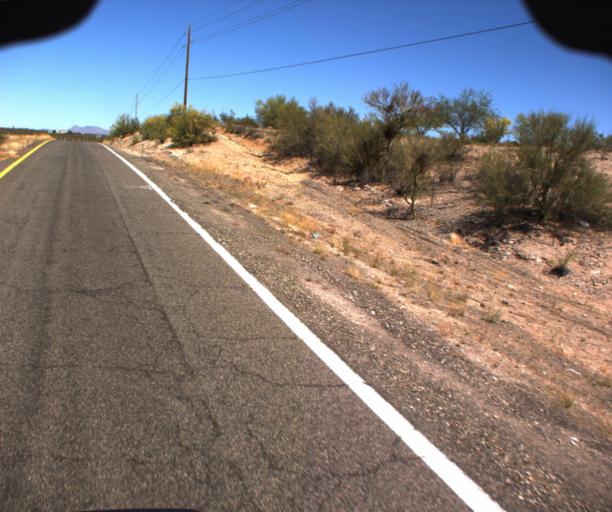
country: US
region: Arizona
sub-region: Maricopa County
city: Wickenburg
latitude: 34.0255
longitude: -112.8084
